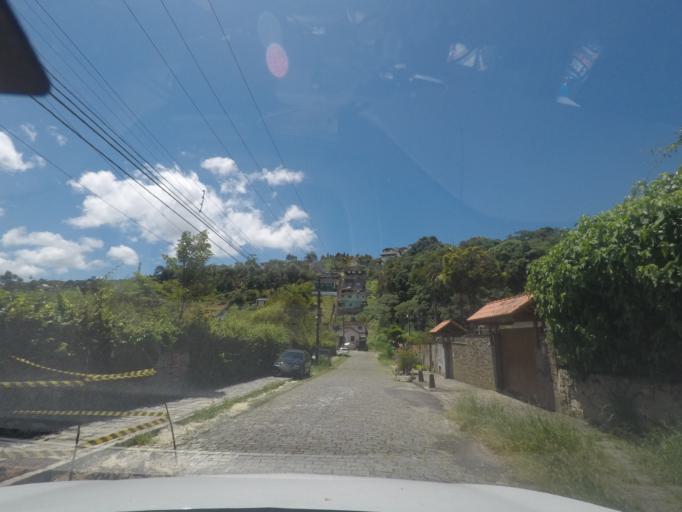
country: BR
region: Rio de Janeiro
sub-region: Teresopolis
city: Teresopolis
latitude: -22.4217
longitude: -42.9822
